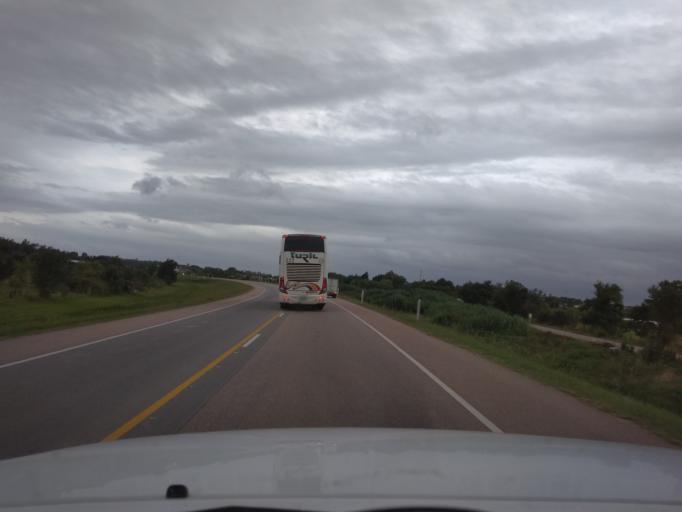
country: UY
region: Canelones
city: Canelones
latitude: -34.5058
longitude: -56.2814
